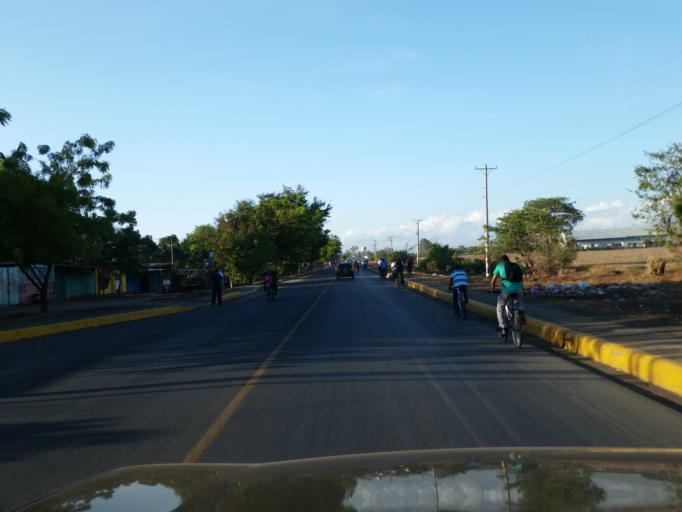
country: NI
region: Managua
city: Tipitapa
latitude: 12.1730
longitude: -86.0947
